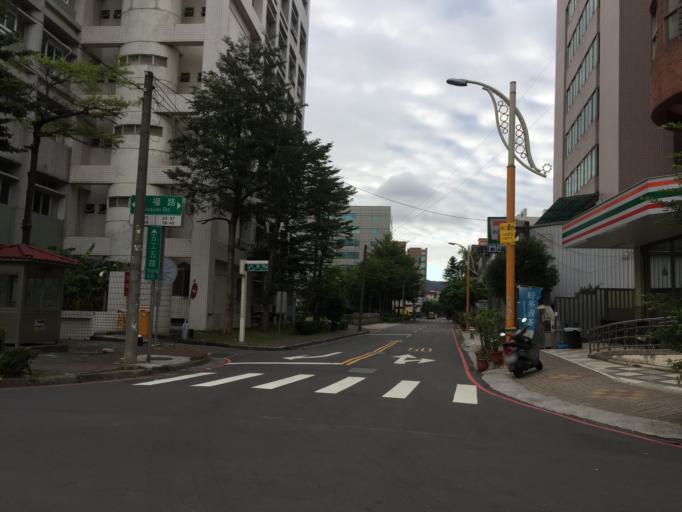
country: TW
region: Taipei
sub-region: Taipei
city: Banqiao
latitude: 25.0664
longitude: 121.4499
